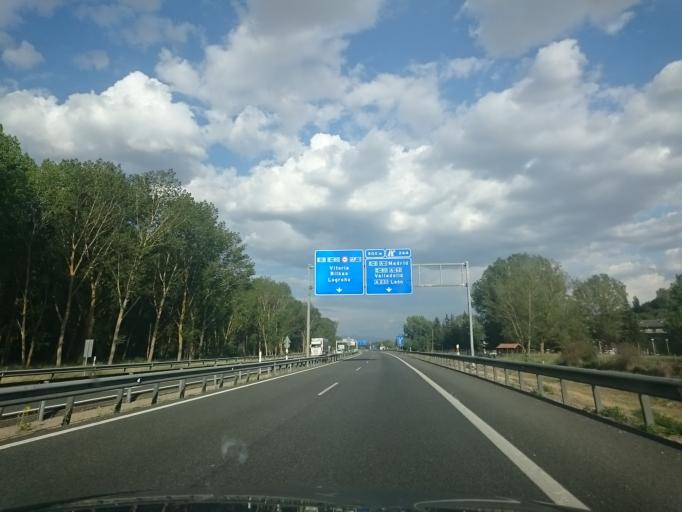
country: ES
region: Castille and Leon
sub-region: Provincia de Burgos
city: Cardenajimeno
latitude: 42.3398
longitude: -3.6337
